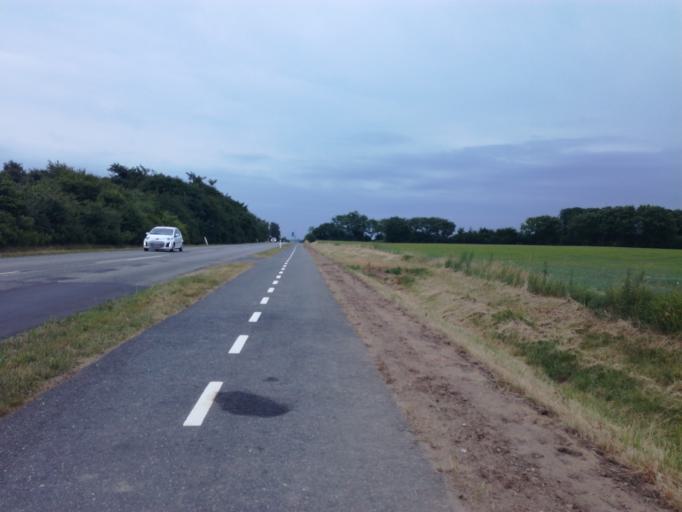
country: DK
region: South Denmark
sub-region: Vejle Kommune
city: Borkop
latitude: 55.6658
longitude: 9.6259
